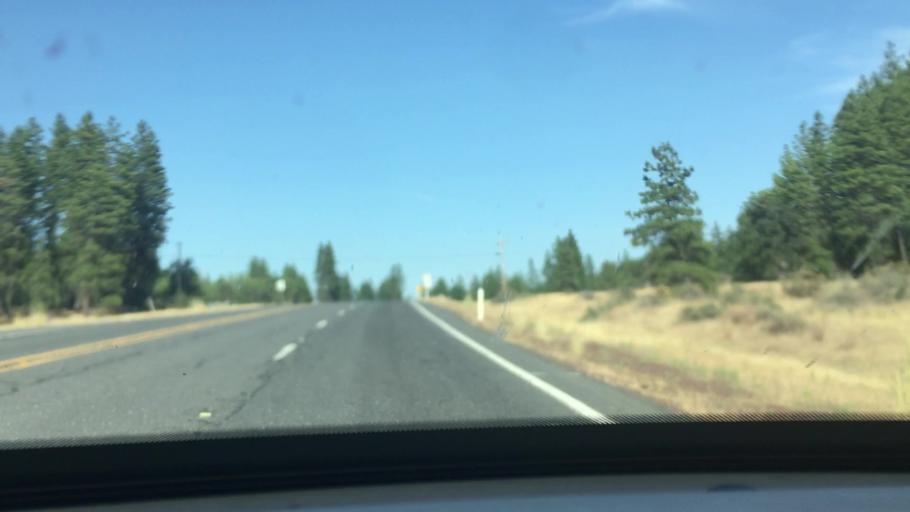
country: US
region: Washington
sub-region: Klickitat County
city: Goldendale
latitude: 45.8972
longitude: -120.7194
